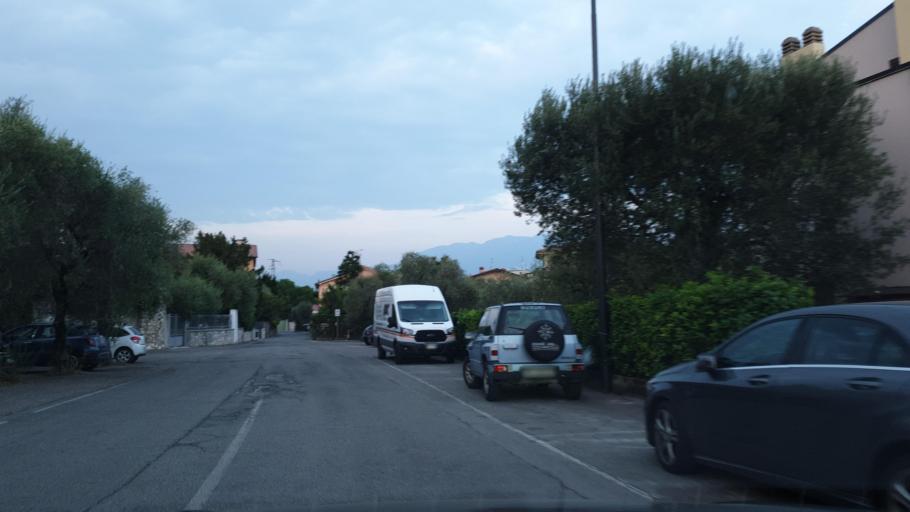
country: IT
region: Lombardy
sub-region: Provincia di Brescia
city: Toscolano Maderno
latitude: 45.6399
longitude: 10.6140
